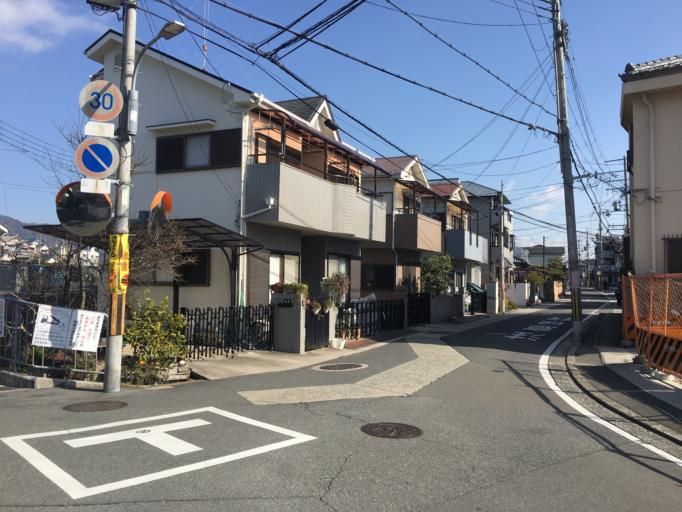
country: JP
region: Osaka
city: Ikeda
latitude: 34.8137
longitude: 135.4499
